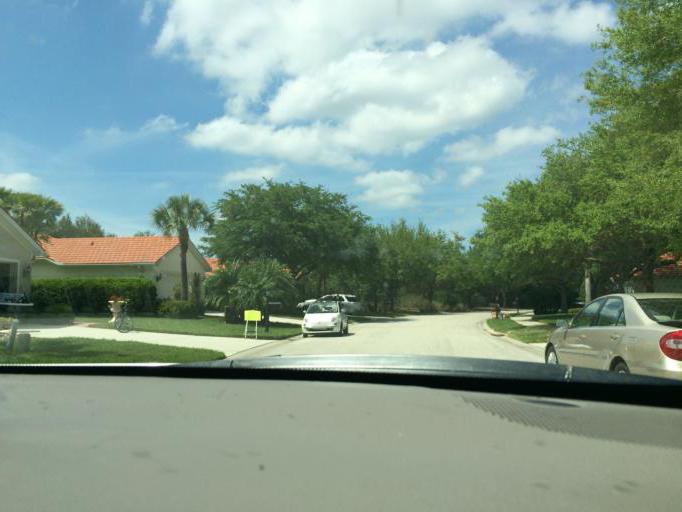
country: US
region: Florida
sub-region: Manatee County
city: Ellenton
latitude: 27.5080
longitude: -82.4474
